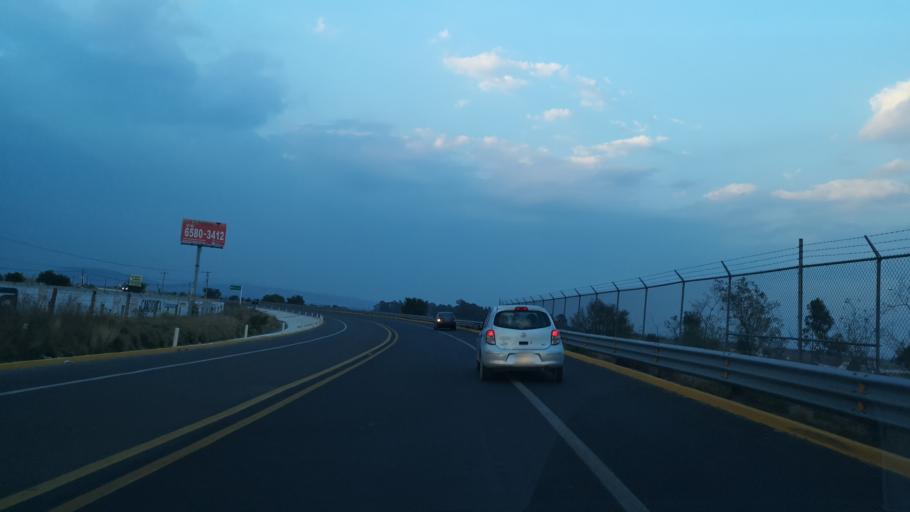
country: MX
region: Puebla
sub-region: Huejotzingo
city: Los Encinos
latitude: 19.1707
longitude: -98.3757
